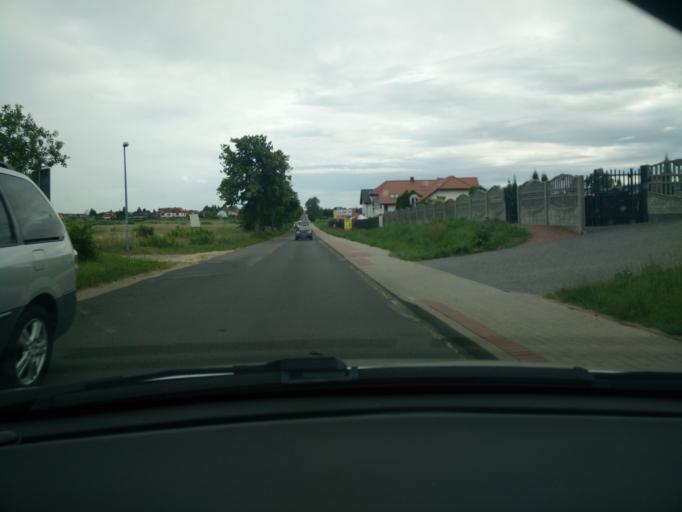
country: PL
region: Pomeranian Voivodeship
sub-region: Powiat pucki
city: Mosty
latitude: 54.6277
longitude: 18.4967
